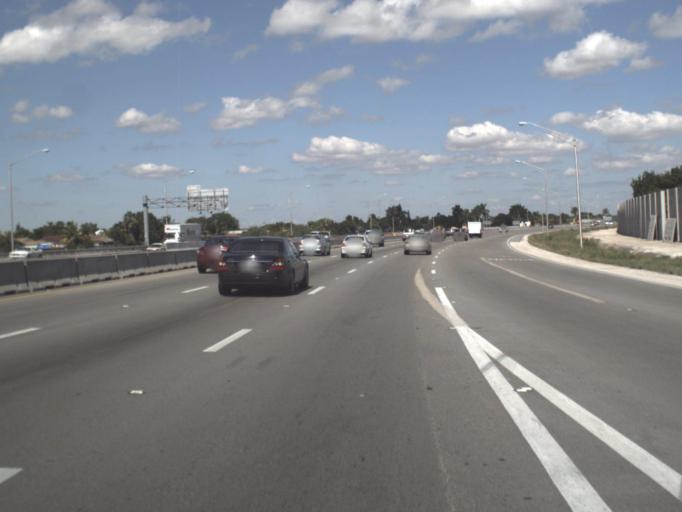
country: US
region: Florida
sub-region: Miami-Dade County
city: South Miami Heights
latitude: 25.6006
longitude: -80.3768
